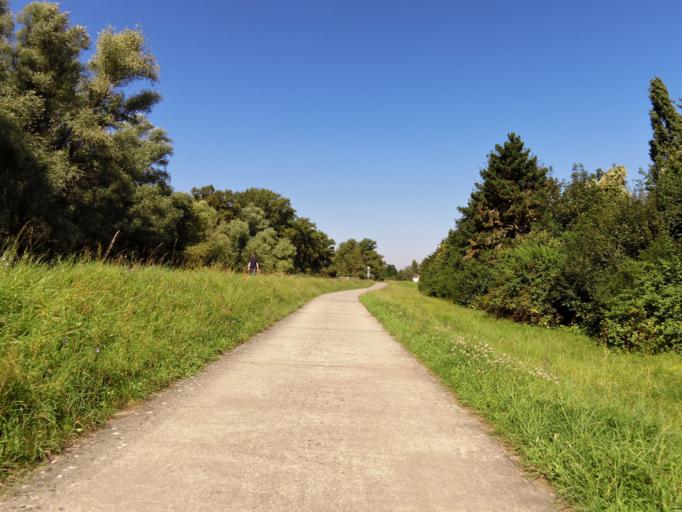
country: DE
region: Hesse
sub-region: Regierungsbezirk Darmstadt
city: Ginsheim-Gustavsburg
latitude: 49.9829
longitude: 8.3226
